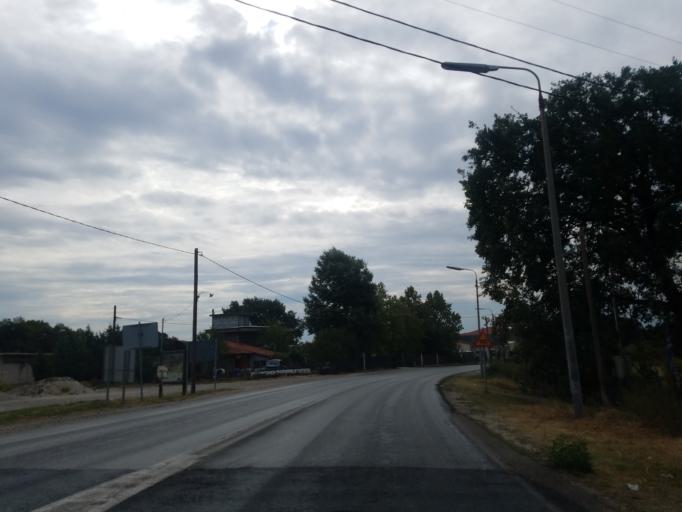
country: GR
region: Thessaly
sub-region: Trikala
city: Kalampaka
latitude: 39.6986
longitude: 21.6394
